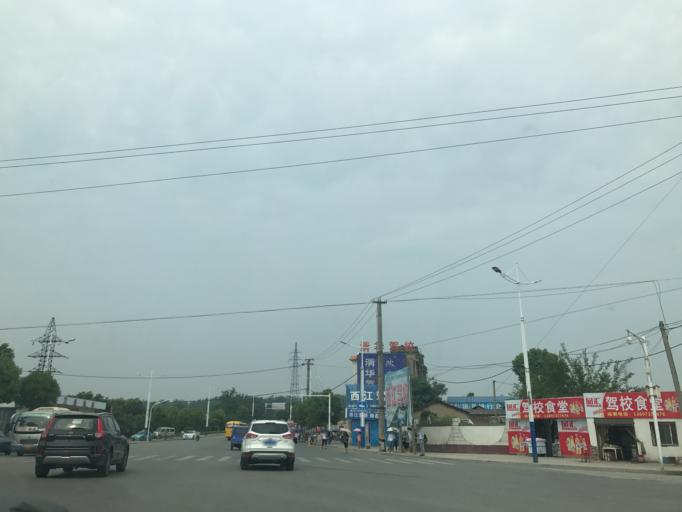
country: CN
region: Hubei
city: Tianmen
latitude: 30.6608
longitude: 113.1347
